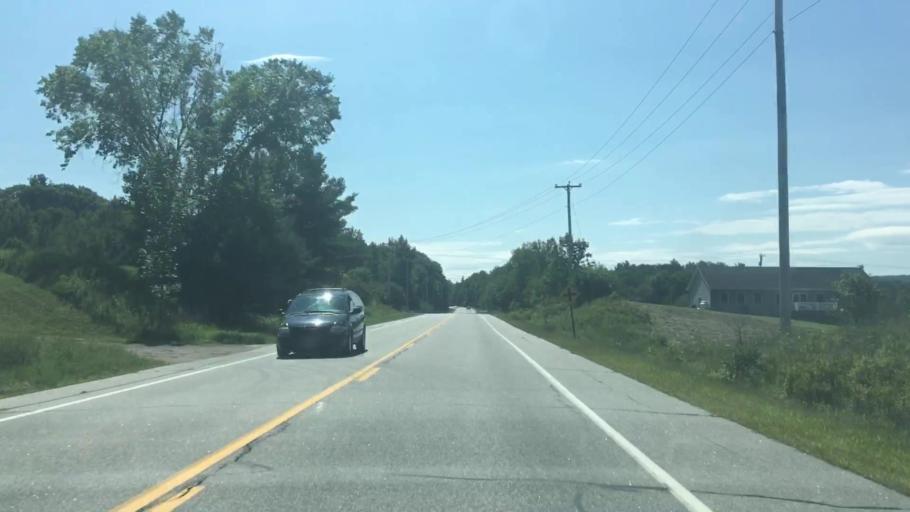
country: US
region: Maine
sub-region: Kennebec County
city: Monmouth
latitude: 44.1631
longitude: -70.0300
